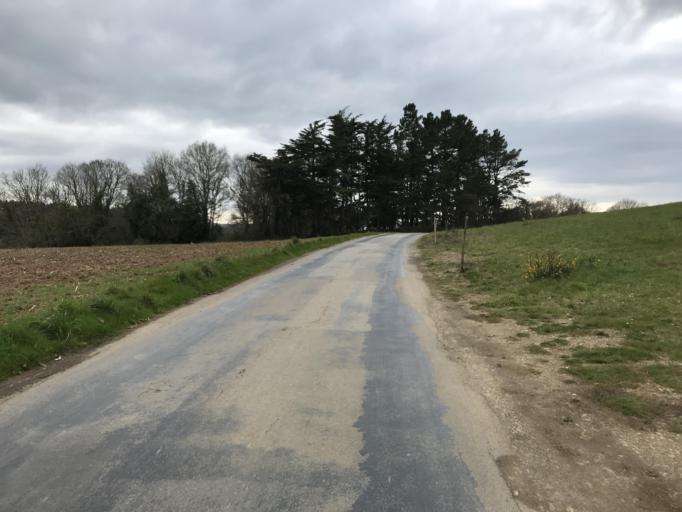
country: FR
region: Brittany
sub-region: Departement du Finistere
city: Hopital-Camfrout
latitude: 48.3194
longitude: -4.2388
